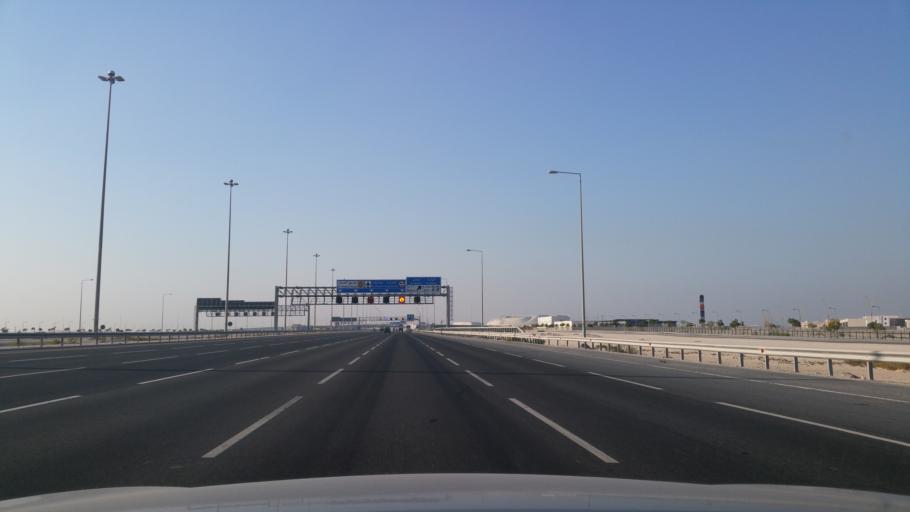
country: QA
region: Al Wakrah
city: Al Wakrah
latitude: 25.1397
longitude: 51.5820
